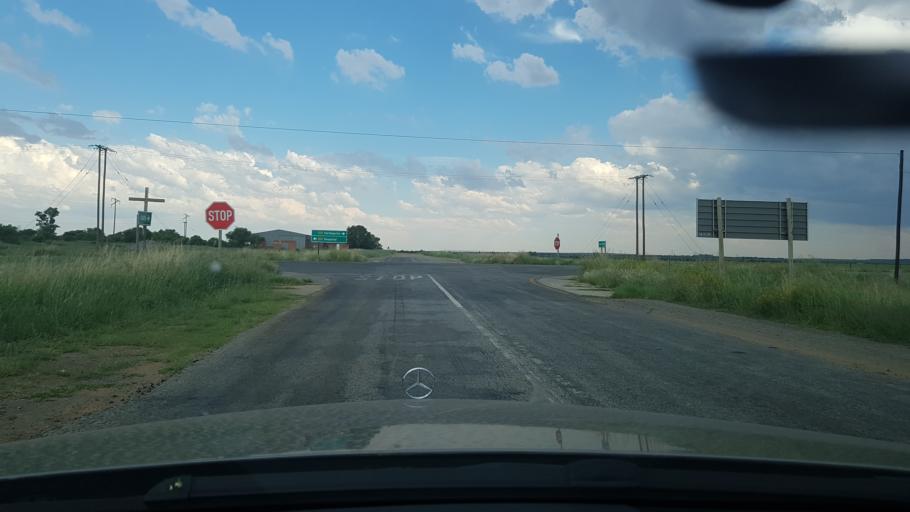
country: ZA
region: Orange Free State
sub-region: Lejweleputswa District Municipality
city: Hoopstad
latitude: -27.9546
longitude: 25.7034
